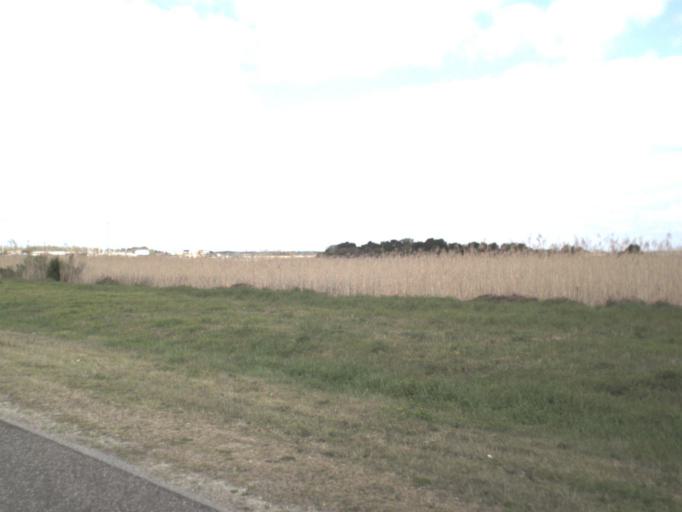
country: US
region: Florida
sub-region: Franklin County
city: Apalachicola
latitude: 29.7262
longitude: -84.9706
